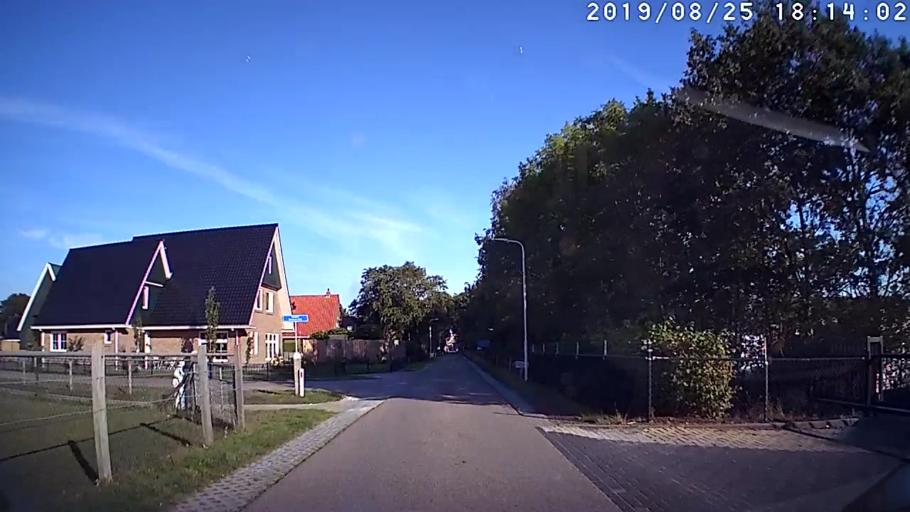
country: NL
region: Friesland
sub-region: Gemeente Gaasterlan-Sleat
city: Oudemirdum
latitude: 52.8562
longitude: 5.5584
